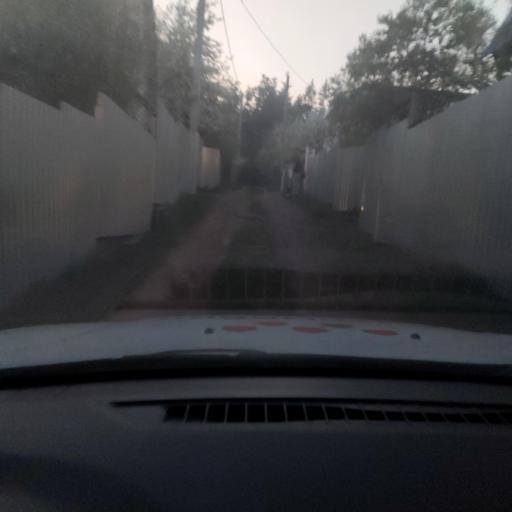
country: RU
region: Bashkortostan
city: Avdon
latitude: 54.6808
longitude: 55.7898
